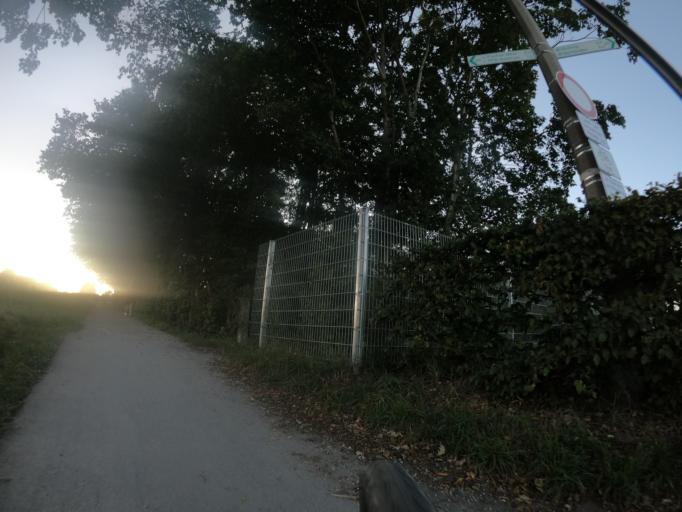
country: DE
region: Bavaria
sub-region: Upper Bavaria
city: Fuerstenfeldbruck
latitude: 48.1898
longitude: 11.2608
